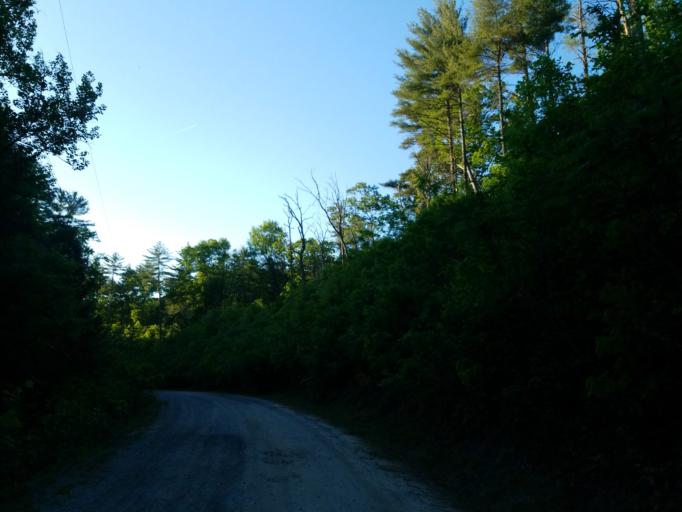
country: US
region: Georgia
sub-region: Fannin County
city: Blue Ridge
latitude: 34.7073
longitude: -84.1487
